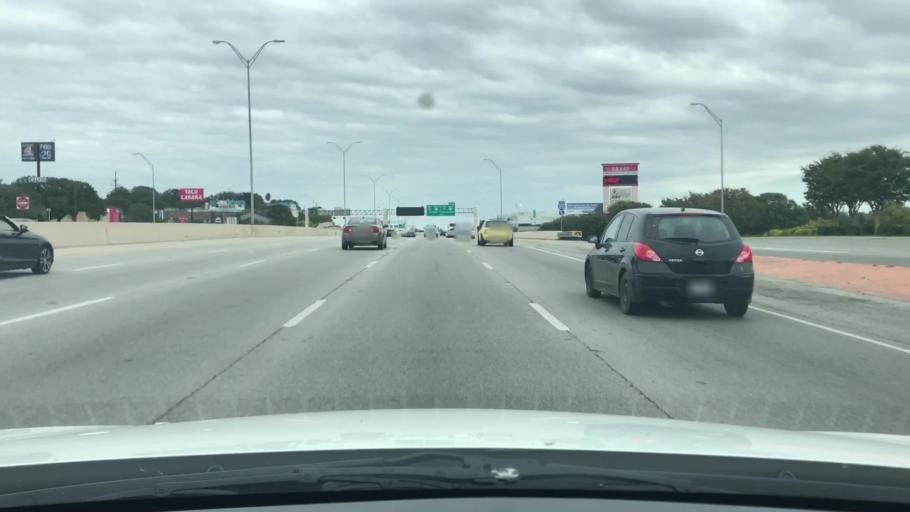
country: US
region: Texas
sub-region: Bexar County
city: Balcones Heights
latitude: 29.4894
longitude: -98.5713
